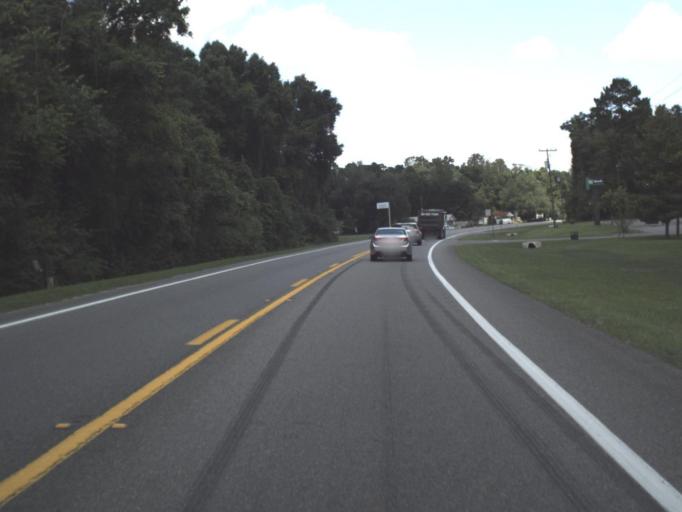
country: US
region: Florida
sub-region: Alachua County
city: High Springs
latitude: 29.9161
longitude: -82.7071
